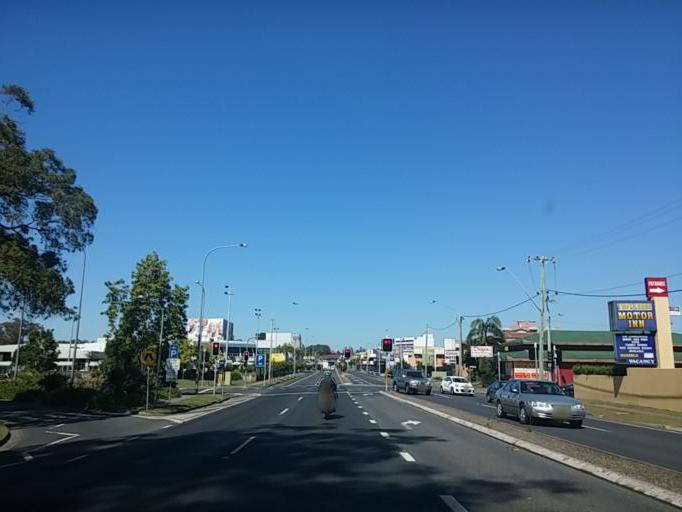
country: AU
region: New South Wales
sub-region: Coffs Harbour
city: Coffs Harbour
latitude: -30.2938
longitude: 153.1163
